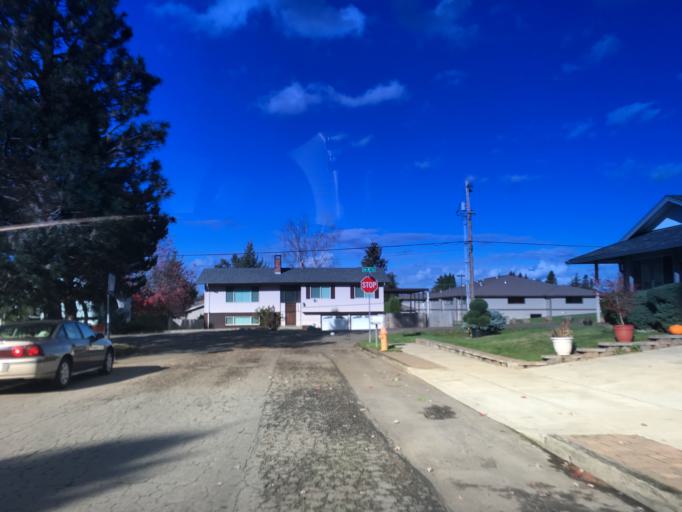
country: US
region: Oregon
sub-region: Multnomah County
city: Troutdale
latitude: 45.5030
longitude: -122.3933
